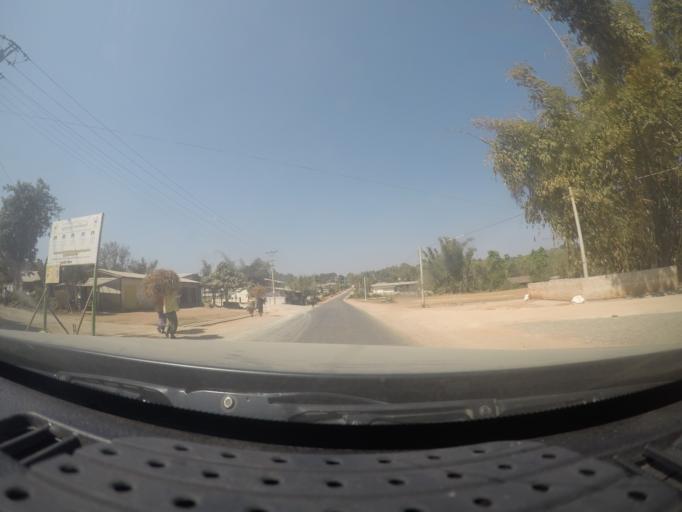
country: MM
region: Shan
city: Taunggyi
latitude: 20.7898
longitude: 96.6457
